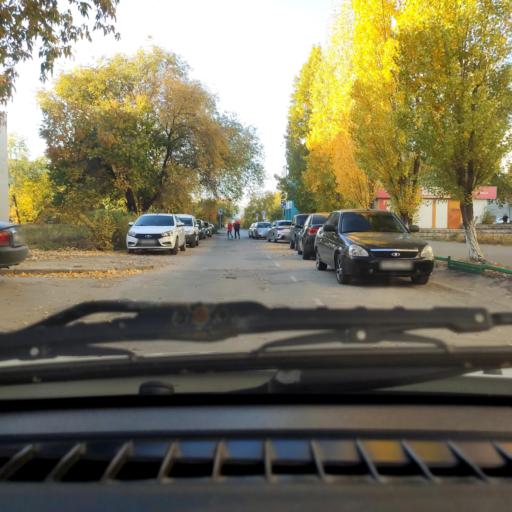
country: RU
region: Samara
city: Zhigulevsk
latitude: 53.4783
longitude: 49.4646
